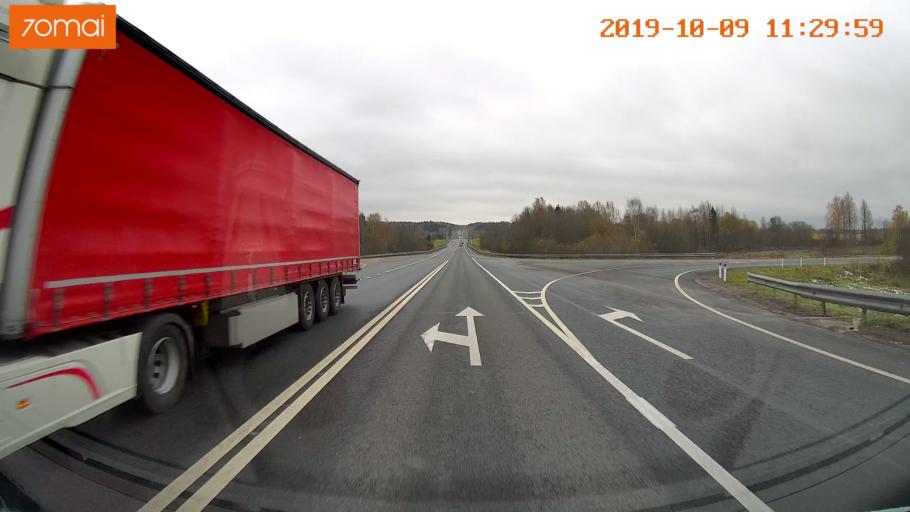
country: RU
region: Vologda
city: Vologda
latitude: 59.0577
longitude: 40.0653
